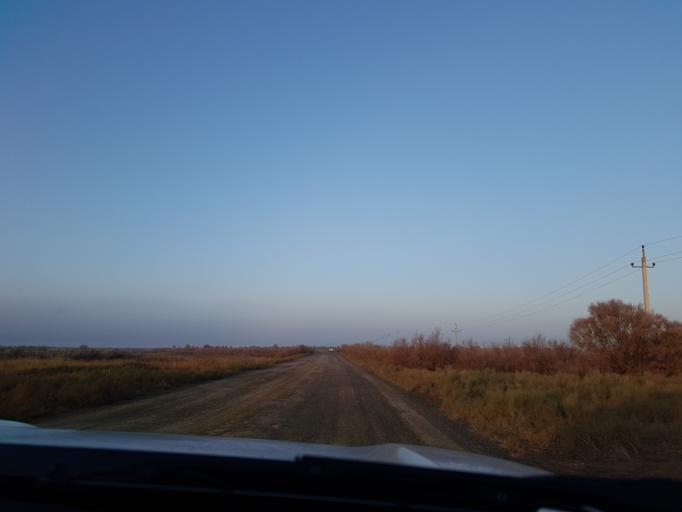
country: TM
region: Dasoguz
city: Koeneuergench
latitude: 41.8450
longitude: 58.6015
